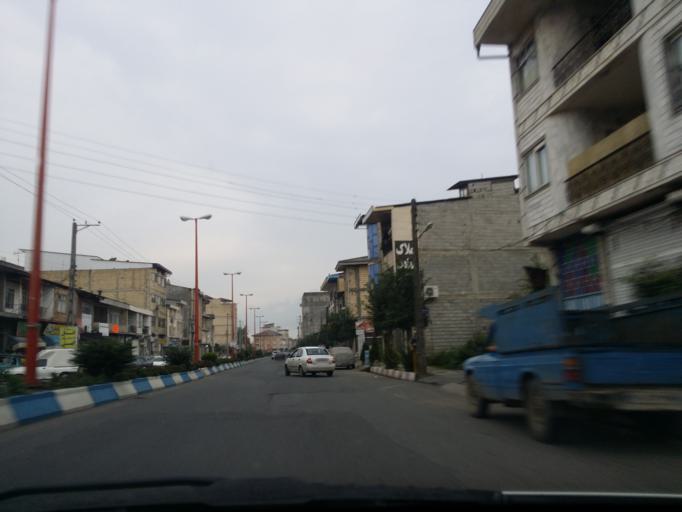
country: IR
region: Mazandaran
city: `Abbasabad
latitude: 36.7193
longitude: 51.1030
